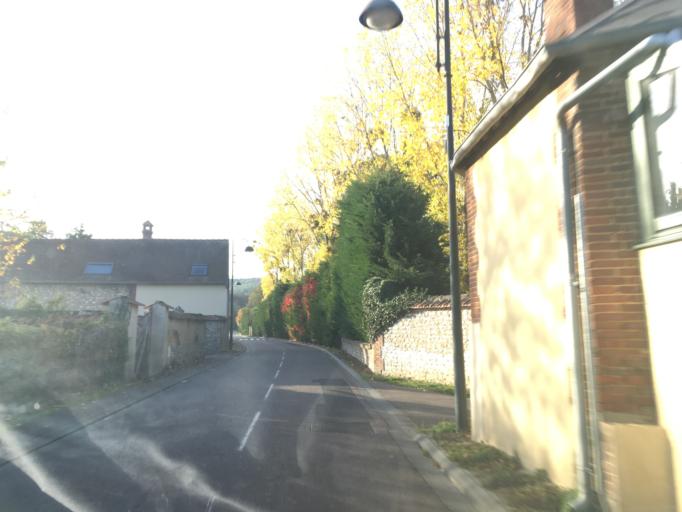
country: FR
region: Haute-Normandie
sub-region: Departement de l'Eure
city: Heudreville-sur-Eure
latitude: 49.1012
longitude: 1.2397
